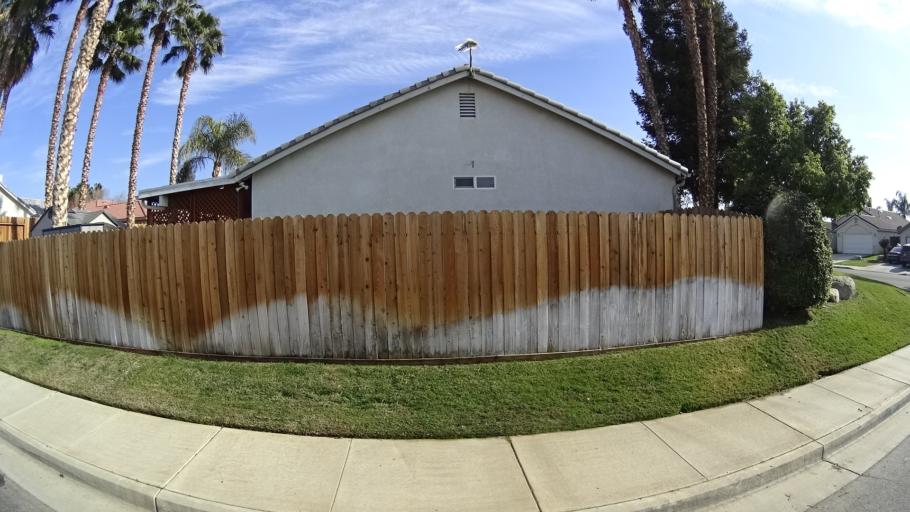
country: US
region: California
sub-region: Kern County
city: Lamont
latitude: 35.3938
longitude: -118.8806
